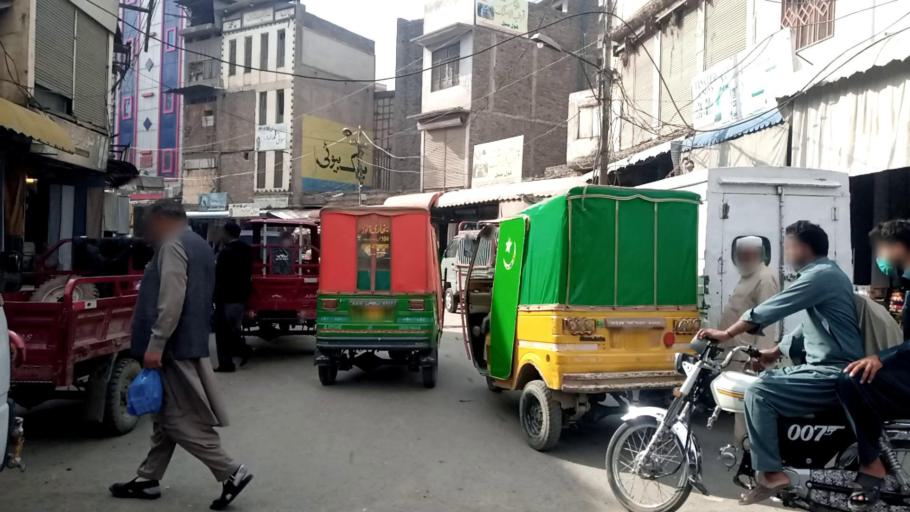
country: PK
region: Khyber Pakhtunkhwa
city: Peshawar
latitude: 34.0085
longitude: 71.5736
